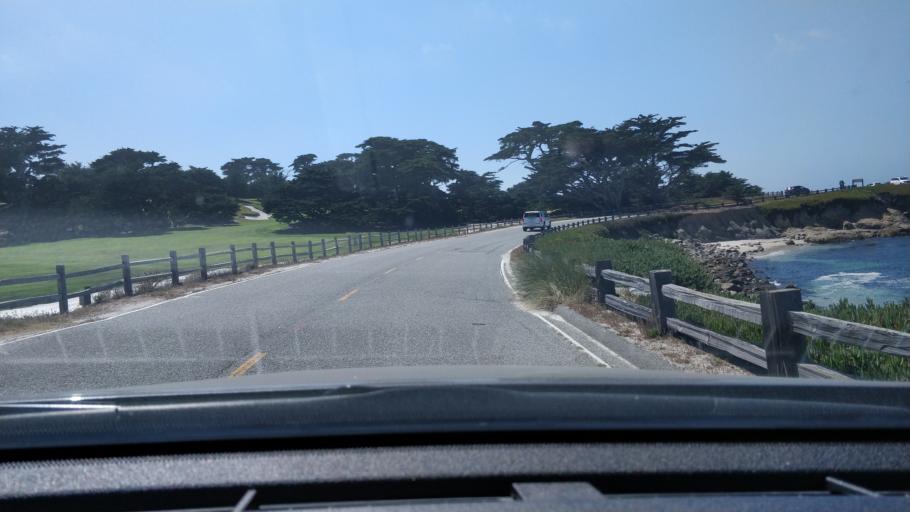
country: US
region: California
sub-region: Monterey County
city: Del Monte Forest
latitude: 36.5821
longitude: -121.9705
